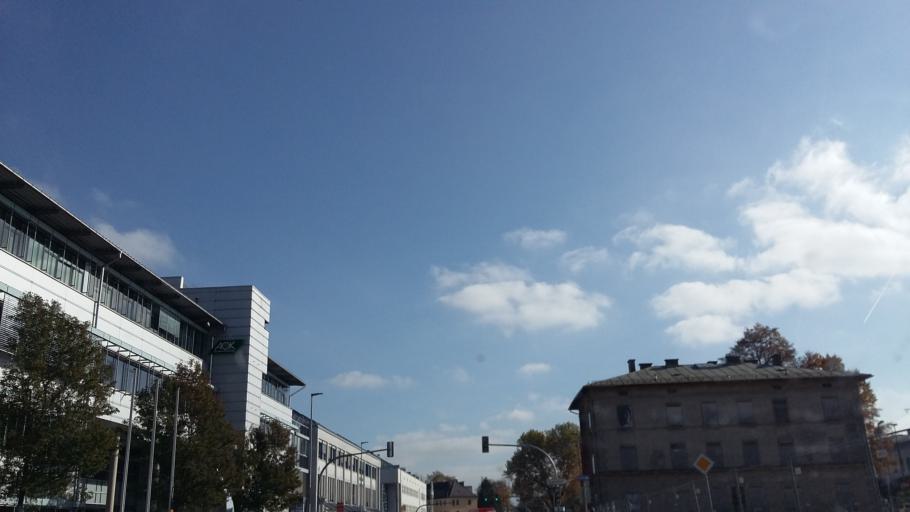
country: DE
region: Bavaria
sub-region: Upper Bavaria
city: Rosenheim
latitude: 47.8515
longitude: 12.1182
